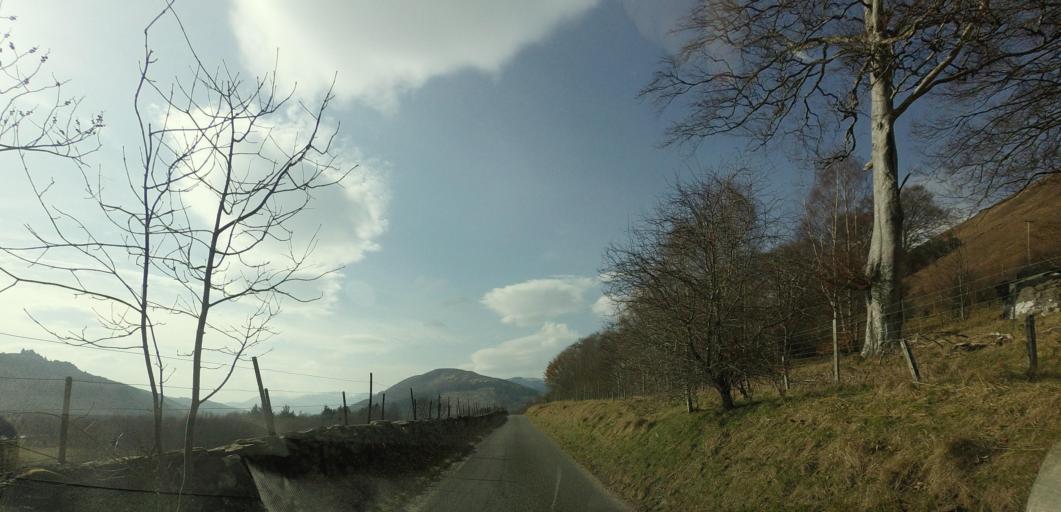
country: GB
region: Scotland
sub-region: Stirling
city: Callander
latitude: 56.5988
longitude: -4.2837
